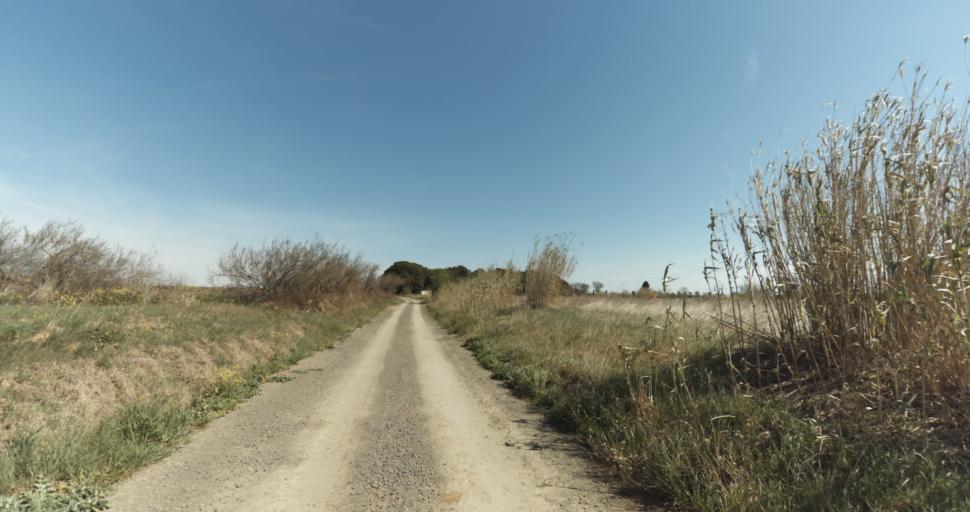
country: FR
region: Languedoc-Roussillon
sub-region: Departement de l'Herault
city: Marseillan
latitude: 43.3845
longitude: 3.5408
